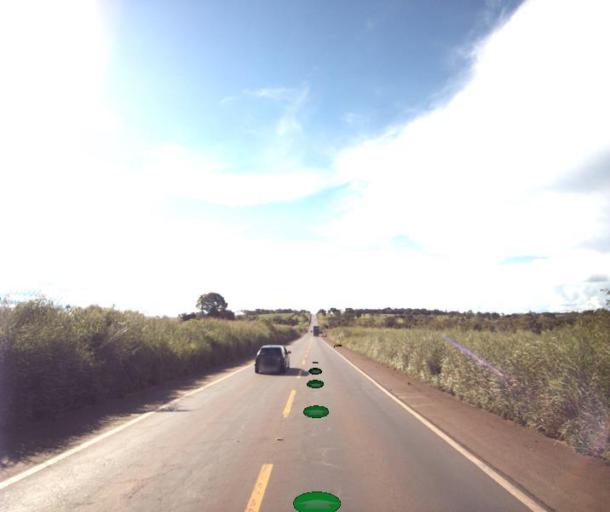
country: BR
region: Goias
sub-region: Rialma
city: Rialma
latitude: -15.3899
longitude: -49.5495
